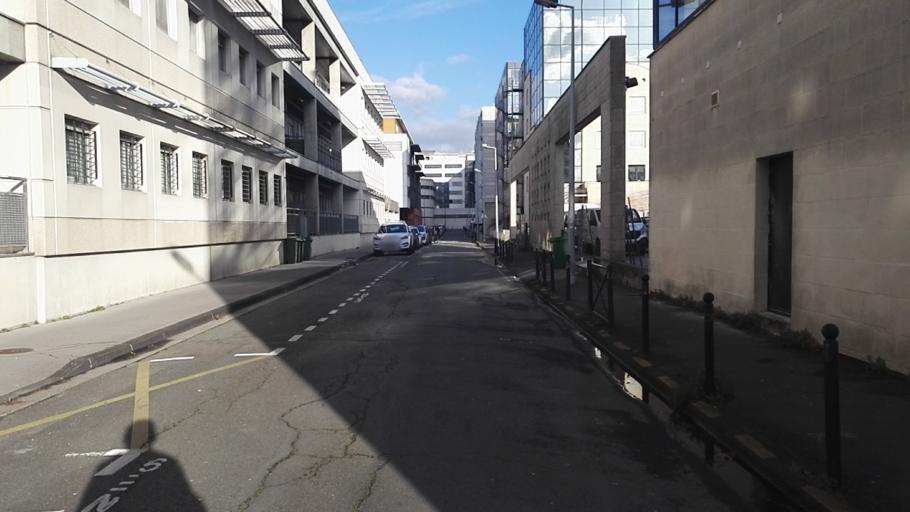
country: FR
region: Aquitaine
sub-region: Departement de la Gironde
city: Bordeaux
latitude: 44.8337
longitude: -0.5923
